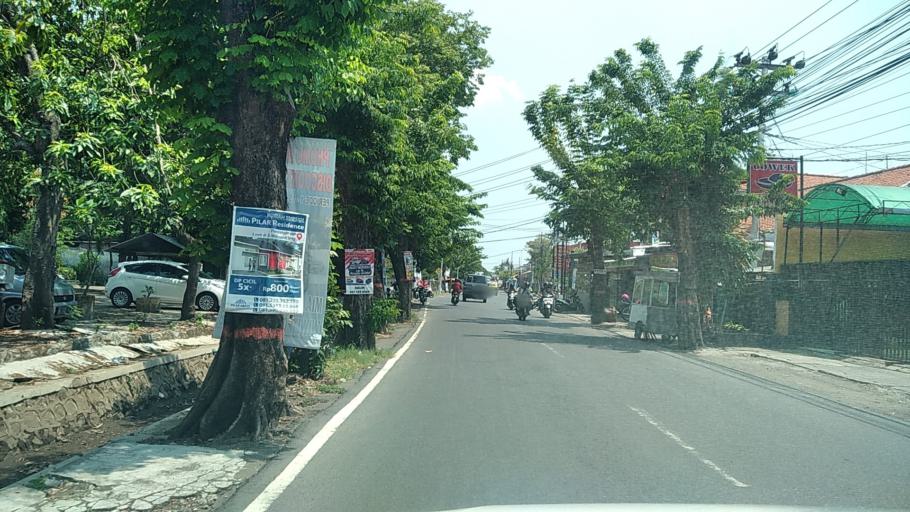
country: ID
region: Central Java
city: Semarang
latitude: -7.0038
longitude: 110.4438
